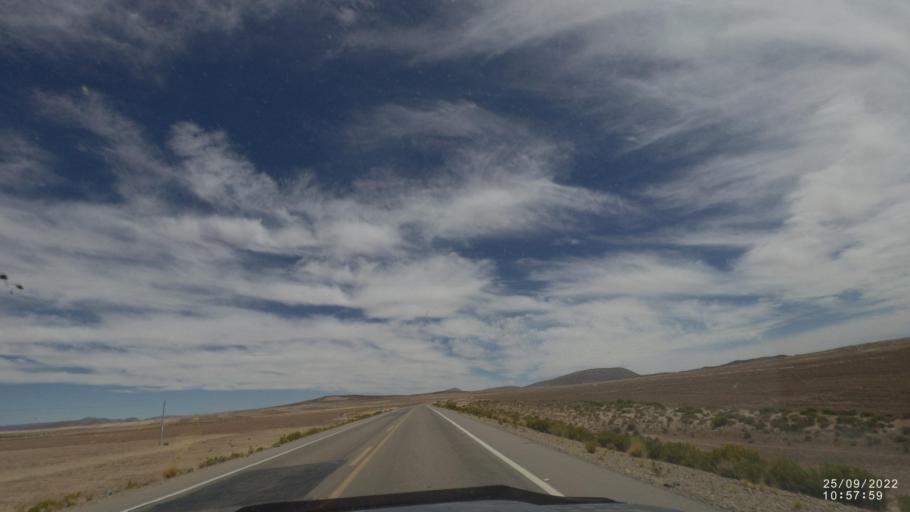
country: BO
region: Oruro
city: Challapata
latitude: -19.4692
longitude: -66.8995
